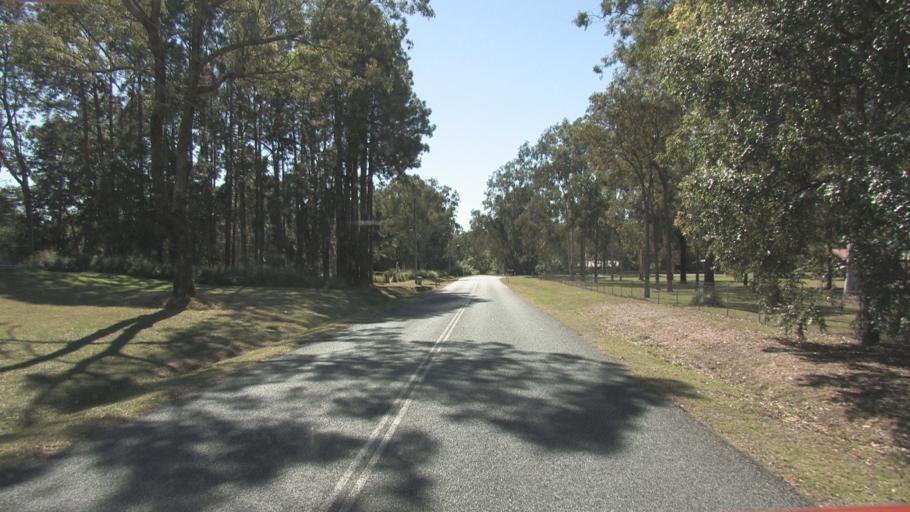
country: AU
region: Queensland
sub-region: Logan
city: Park Ridge South
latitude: -27.7053
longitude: 153.0586
